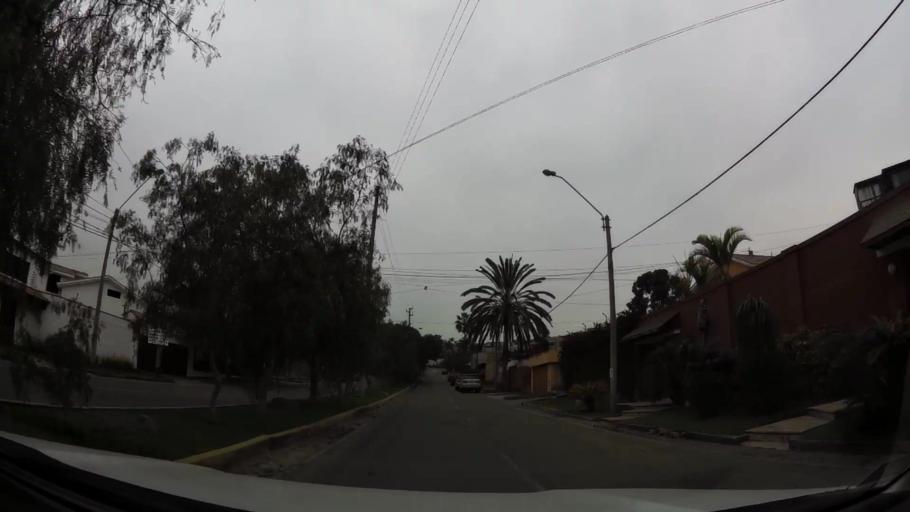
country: PE
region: Lima
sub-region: Lima
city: La Molina
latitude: -12.0838
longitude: -76.9175
